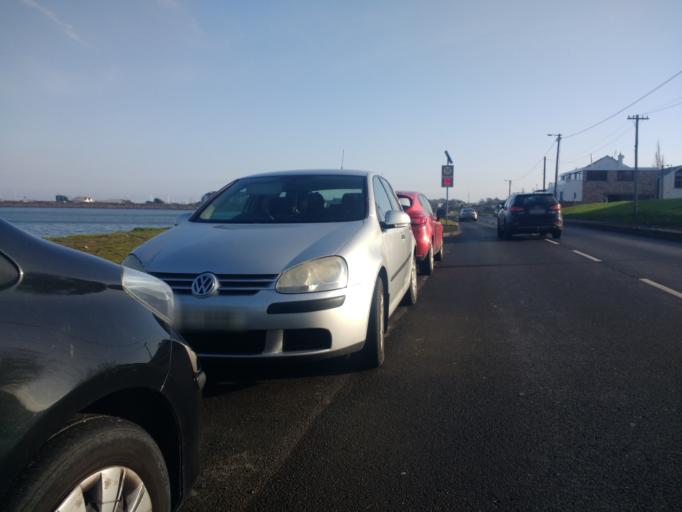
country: IE
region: Leinster
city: Malahide
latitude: 53.4549
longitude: -6.1646
